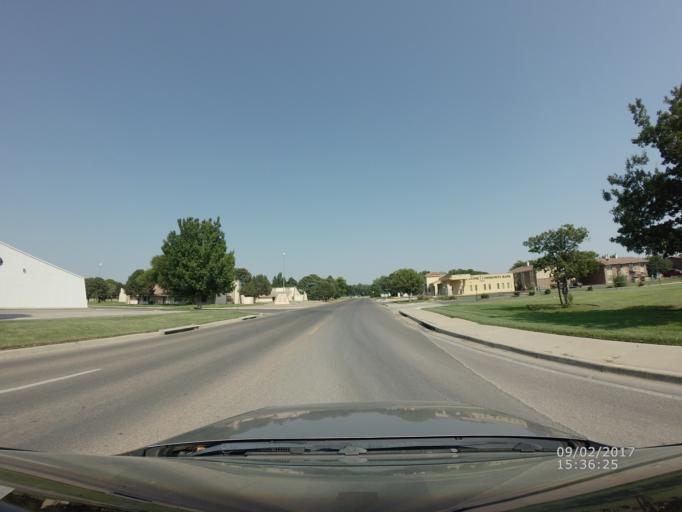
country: US
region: New Mexico
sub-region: Curry County
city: Clovis
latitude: 34.4391
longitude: -103.1961
